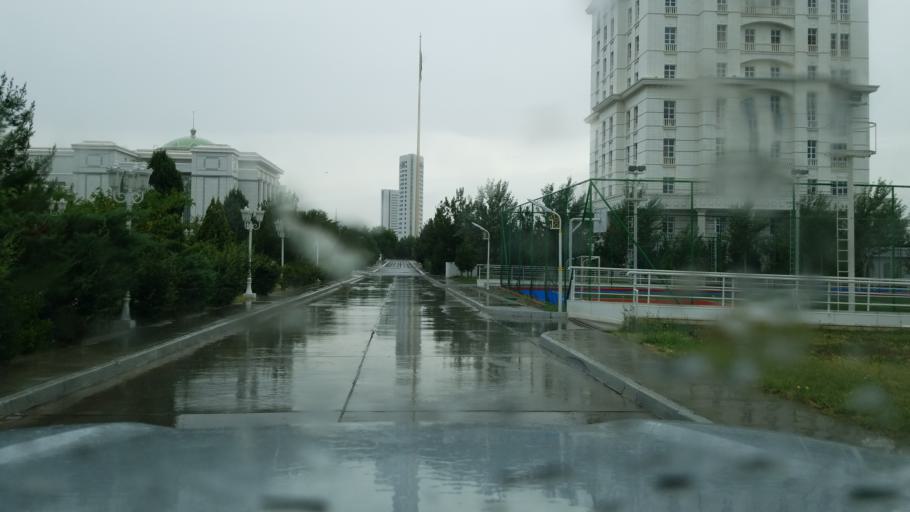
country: TM
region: Ahal
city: Ashgabat
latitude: 37.8849
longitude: 58.3544
